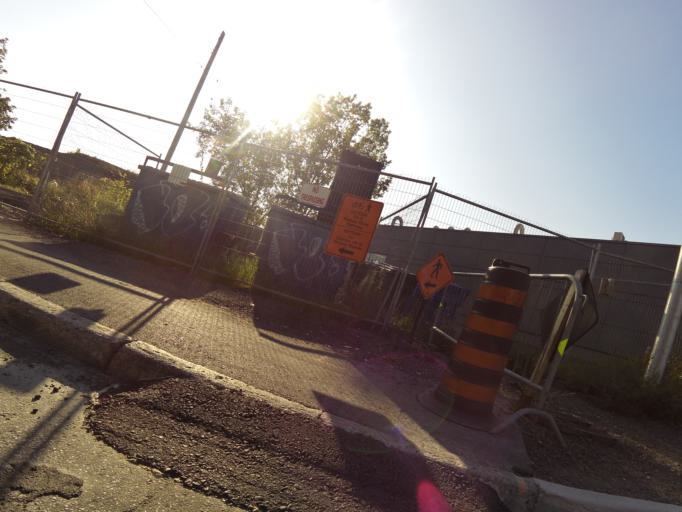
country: CA
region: Ontario
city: Ottawa
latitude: 45.4116
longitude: -75.6642
